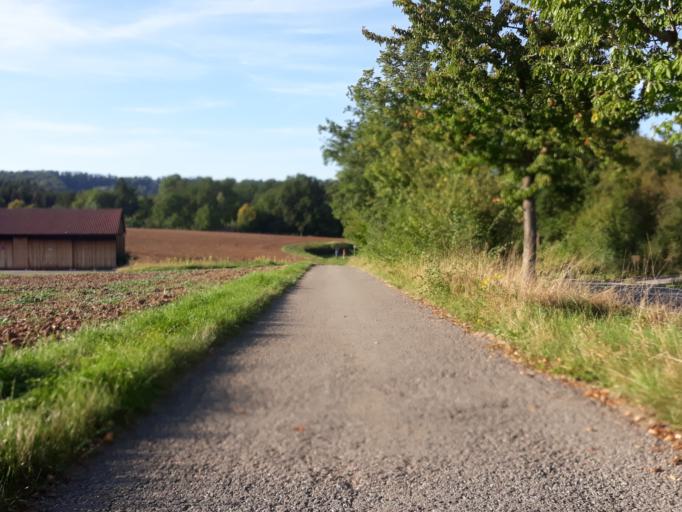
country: DE
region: Baden-Wuerttemberg
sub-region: Regierungsbezirk Stuttgart
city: Schonaich
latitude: 48.6489
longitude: 9.0487
